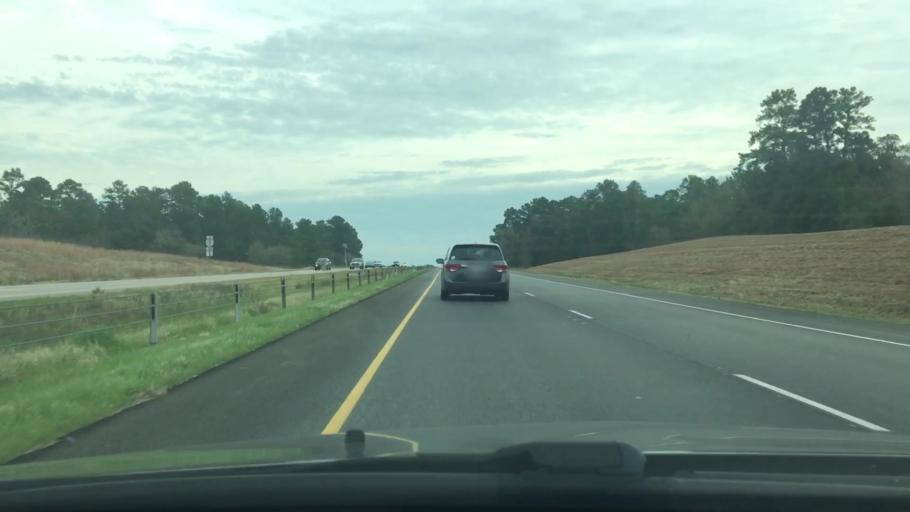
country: US
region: Texas
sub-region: Madison County
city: Madisonville
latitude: 30.8802
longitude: -95.7659
